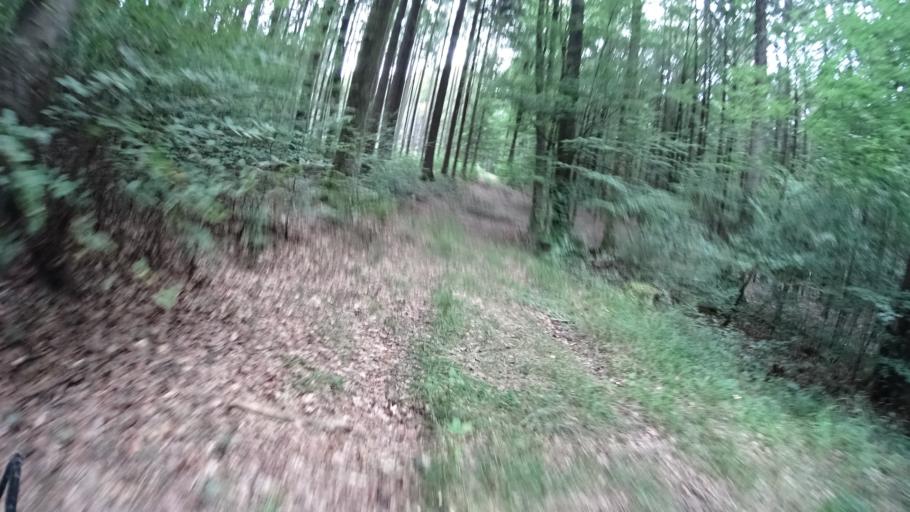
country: DE
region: Bavaria
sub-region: Upper Bavaria
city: Walting
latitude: 48.9149
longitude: 11.3325
